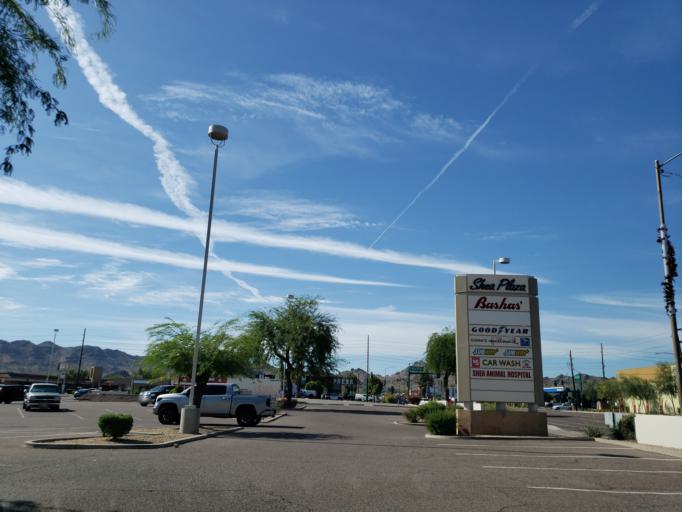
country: US
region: Arizona
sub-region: Maricopa County
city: Paradise Valley
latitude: 33.5886
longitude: -112.0110
